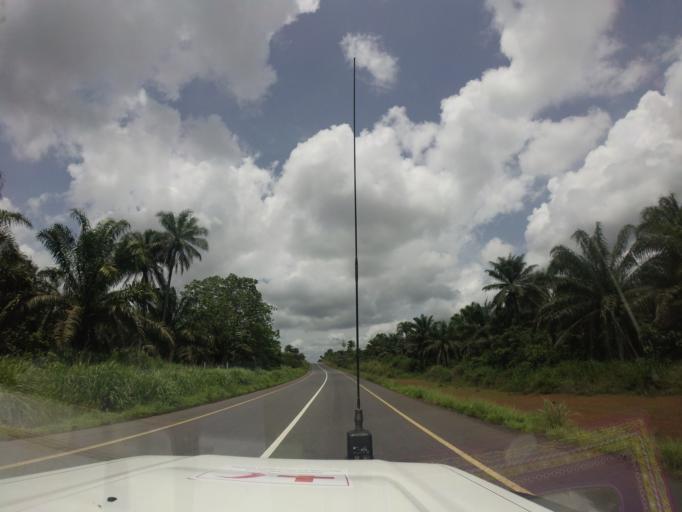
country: SL
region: Northern Province
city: Mange
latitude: 9.0165
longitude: -12.8721
